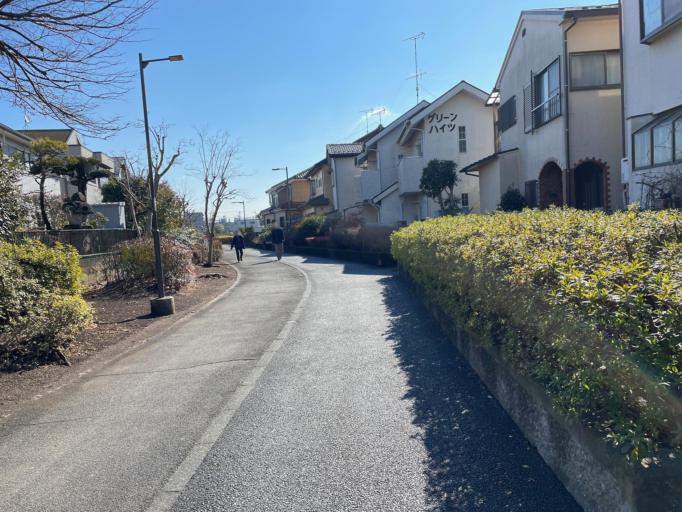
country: JP
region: Tokyo
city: Kokubunji
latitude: 35.6606
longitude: 139.4709
